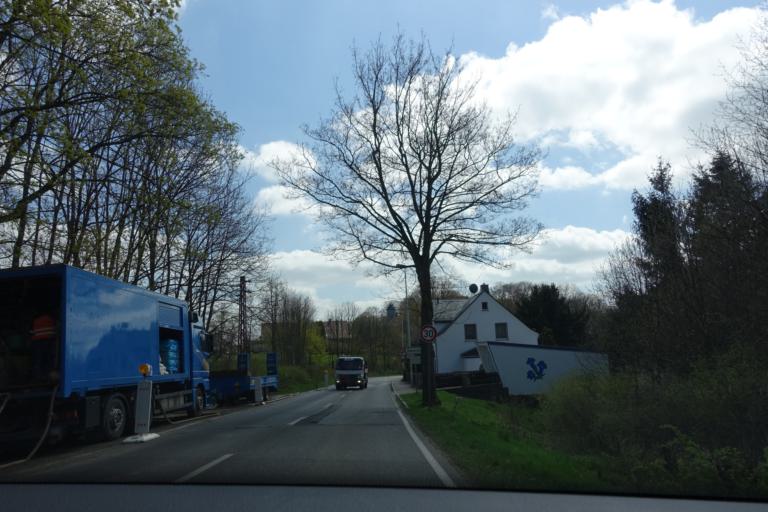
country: DE
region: Saxony
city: Limbach-Oberfrohna
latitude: 50.8352
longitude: 12.8197
